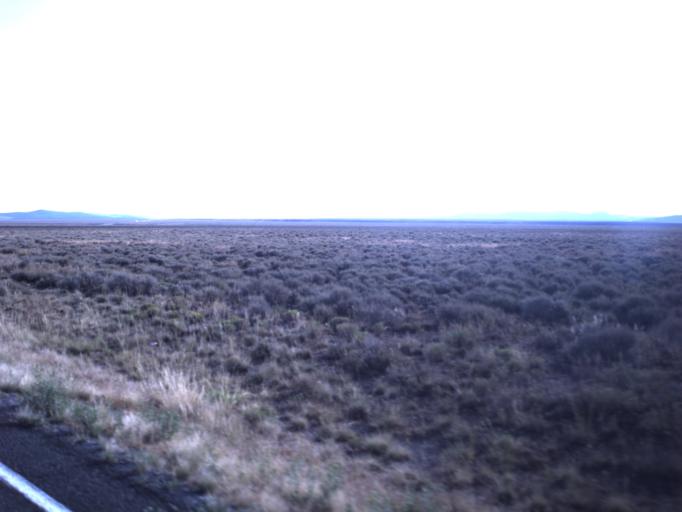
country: US
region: Utah
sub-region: Iron County
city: Enoch
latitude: 37.9237
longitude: -113.0315
